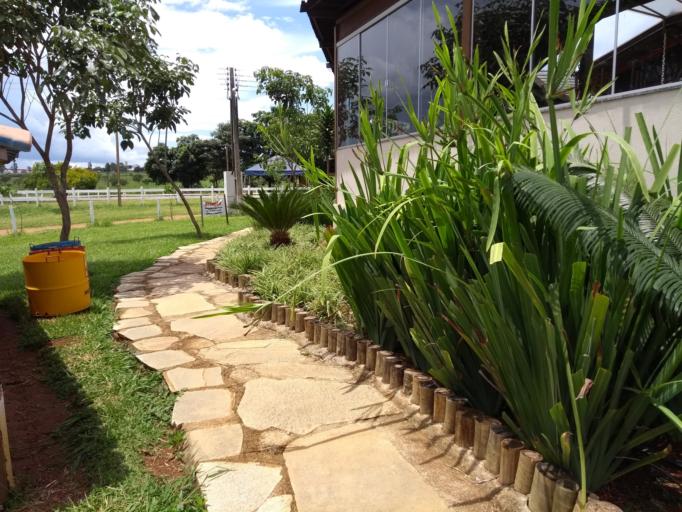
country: BR
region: Federal District
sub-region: Brasilia
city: Brasilia
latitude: -15.6605
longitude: -47.7717
